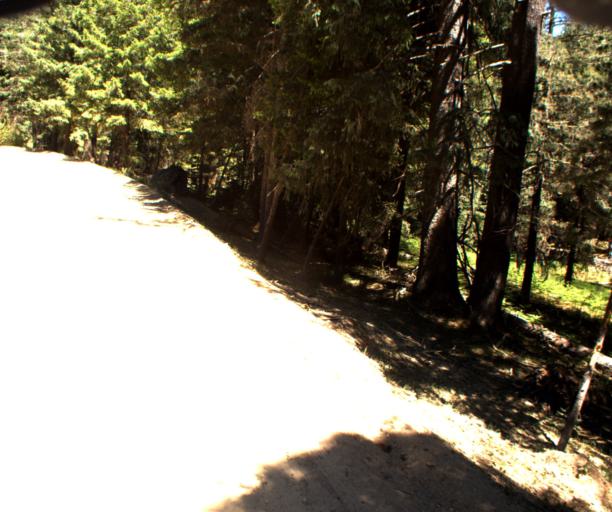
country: US
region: Arizona
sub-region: Graham County
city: Swift Trail Junction
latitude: 32.6722
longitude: -109.8851
